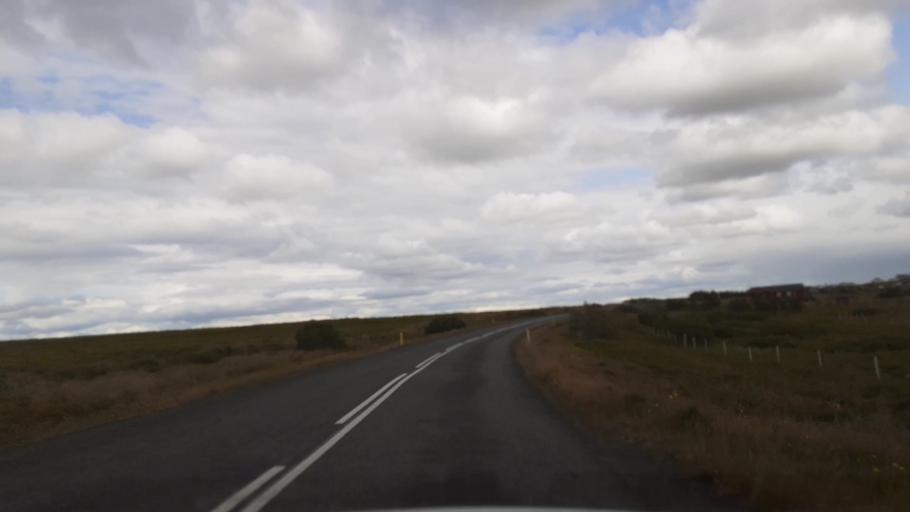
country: IS
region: South
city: Vestmannaeyjar
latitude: 63.8256
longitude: -20.4282
